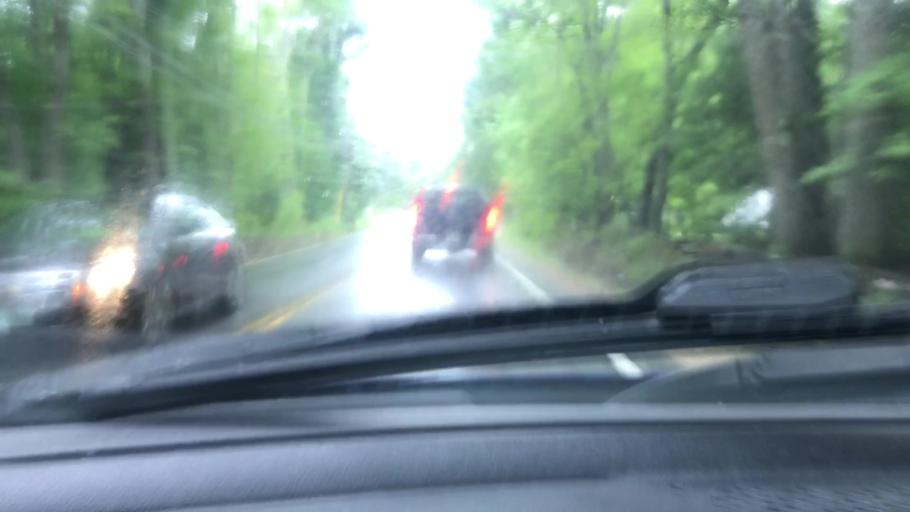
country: US
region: New Hampshire
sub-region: Rockingham County
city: Candia
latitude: 43.1644
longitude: -71.2450
